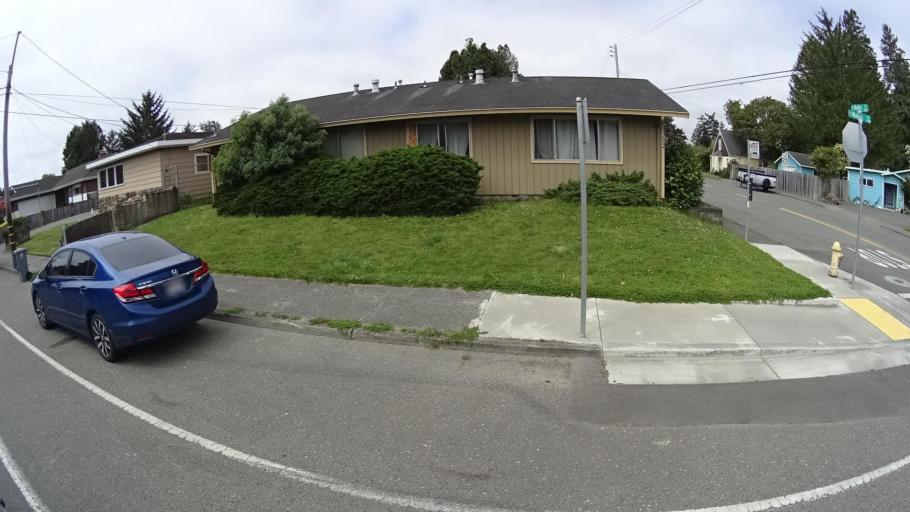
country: US
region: California
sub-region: Humboldt County
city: Cutten
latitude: 40.7640
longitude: -124.1456
